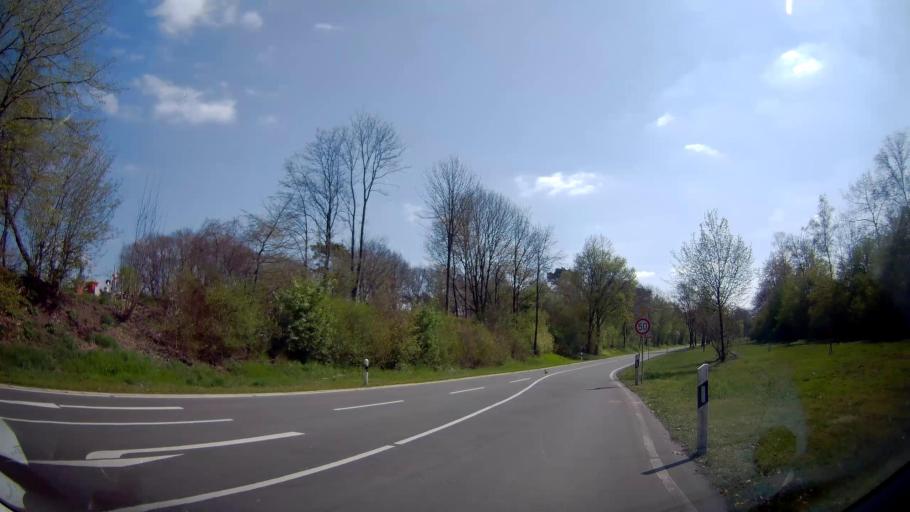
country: DE
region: North Rhine-Westphalia
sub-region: Regierungsbezirk Munster
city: Klein Reken
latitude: 51.7360
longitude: 7.0459
